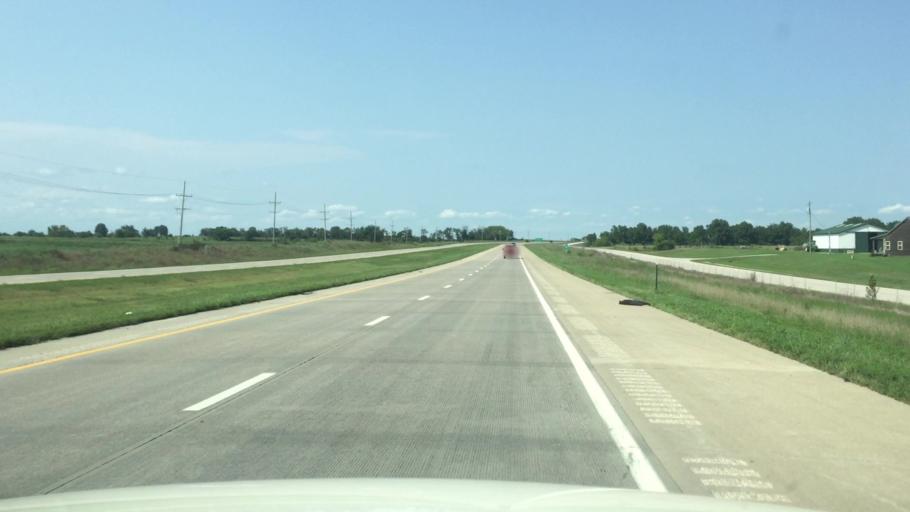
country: US
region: Kansas
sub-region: Linn County
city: Pleasanton
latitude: 38.2022
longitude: -94.7053
